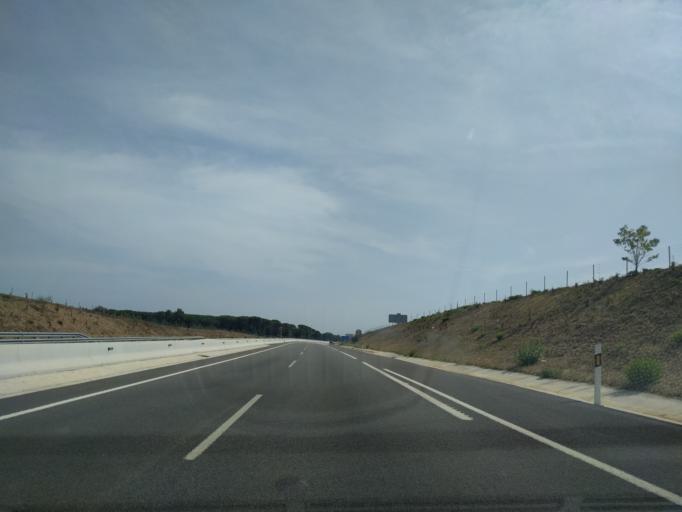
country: ES
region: Catalonia
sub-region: Provincia de Girona
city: Sils
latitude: 41.8303
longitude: 2.7604
